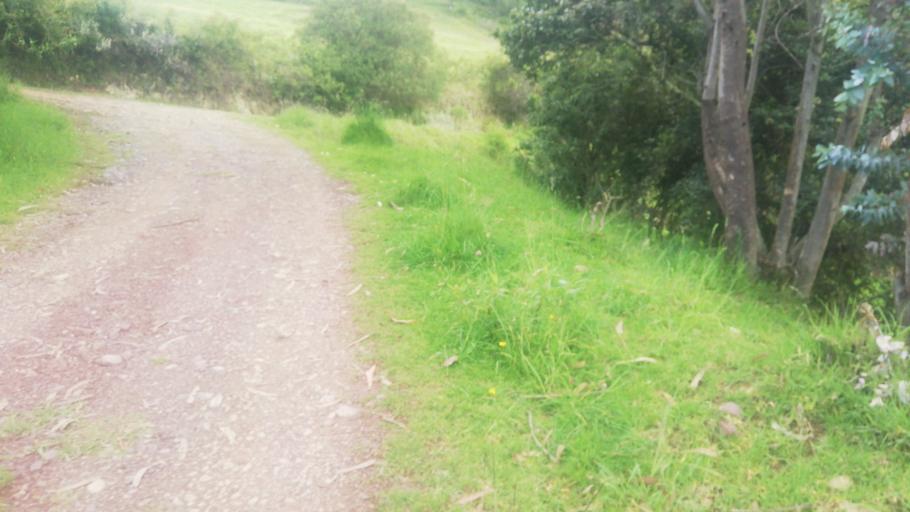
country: CO
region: Boyaca
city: Socha Viejo
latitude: 6.0725
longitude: -72.7303
